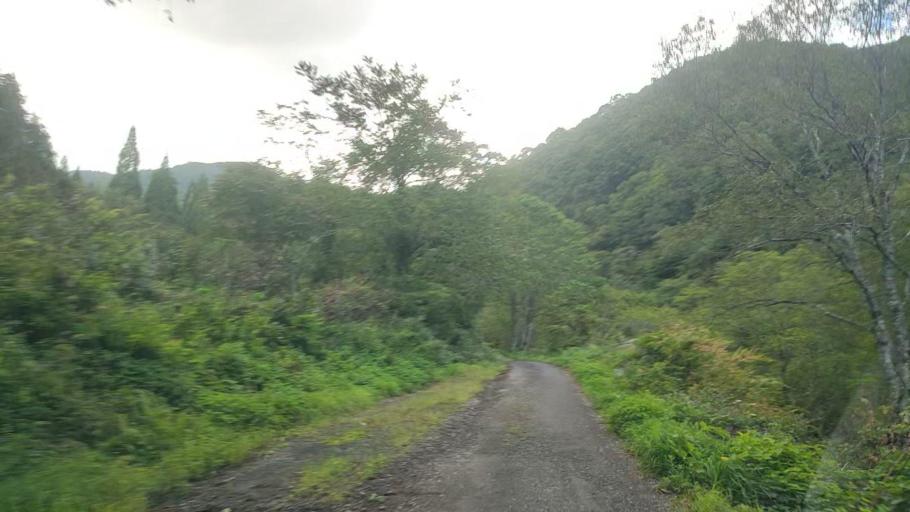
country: JP
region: Toyama
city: Yatsuomachi-higashikumisaka
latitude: 36.3286
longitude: 137.0784
